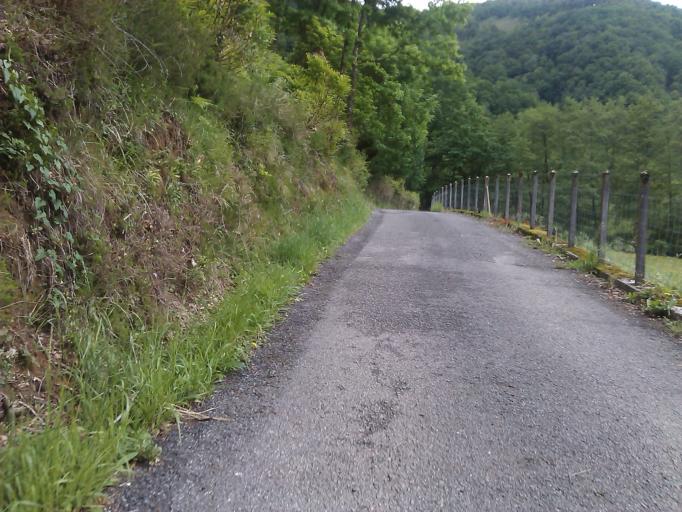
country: ES
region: Navarre
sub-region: Provincia de Navarra
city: Areso
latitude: 43.1079
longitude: -1.9384
